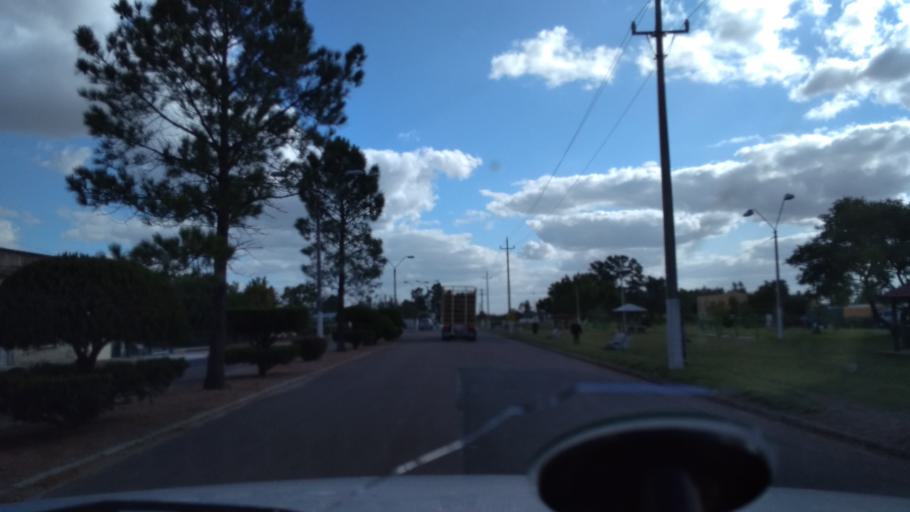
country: UY
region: Florida
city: Casupa
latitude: -34.1010
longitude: -55.6543
